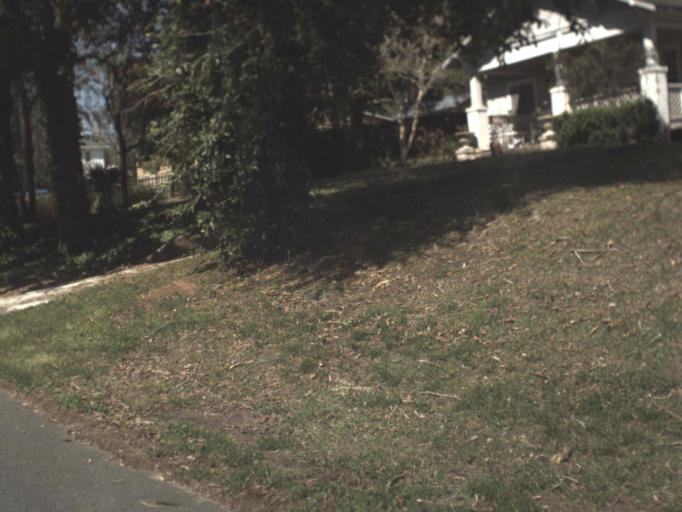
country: US
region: Florida
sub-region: Gadsden County
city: Quincy
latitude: 30.5913
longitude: -84.5698
